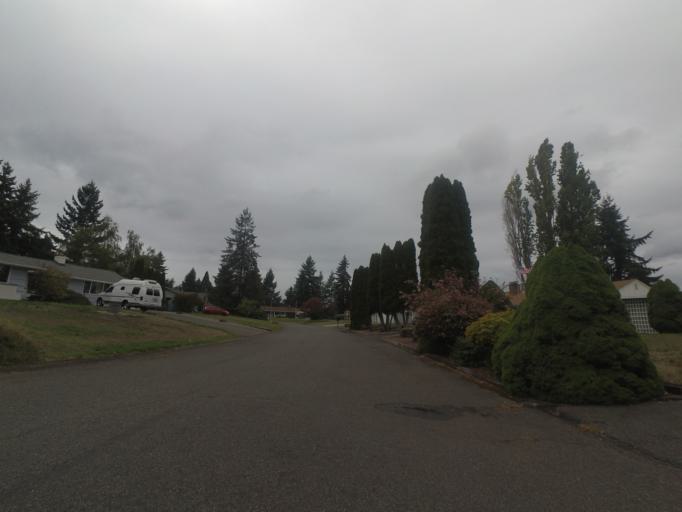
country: US
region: Washington
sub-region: Pierce County
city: Lakewood
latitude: 47.1523
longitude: -122.5078
